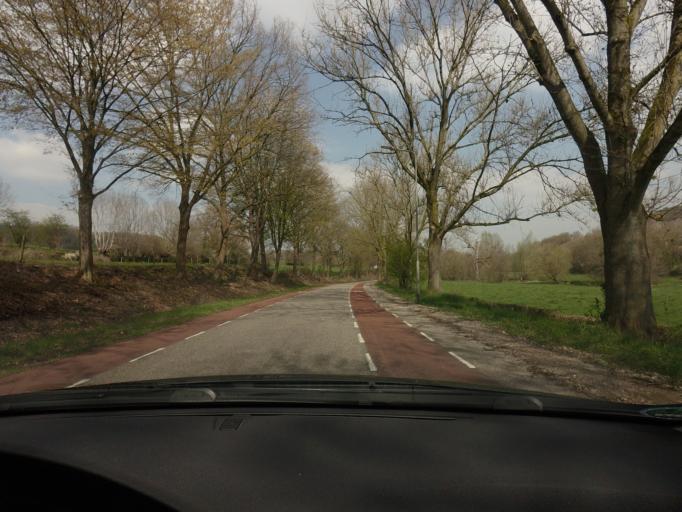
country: BE
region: Flanders
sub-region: Provincie Limburg
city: Sint-Pieters-Voeren
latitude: 50.7759
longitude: 5.8543
